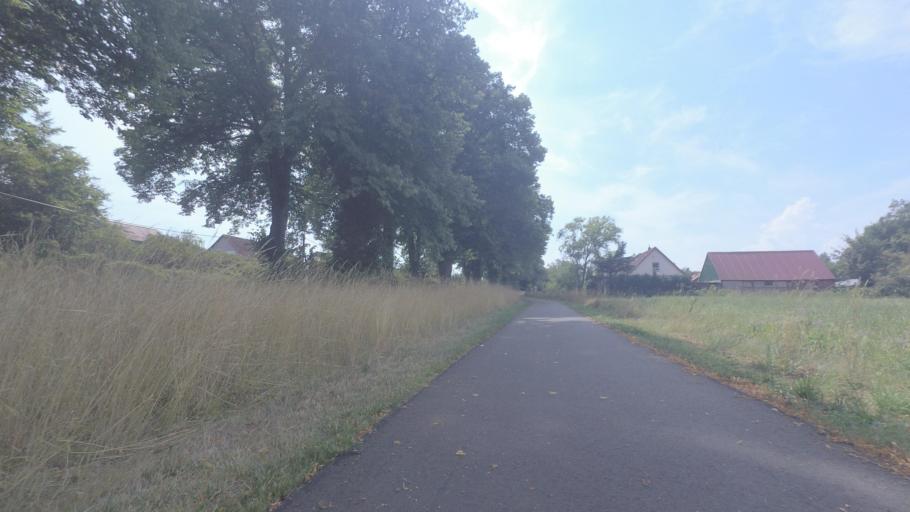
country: DE
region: Mecklenburg-Vorpommern
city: Garz
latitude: 54.2496
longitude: 13.3437
